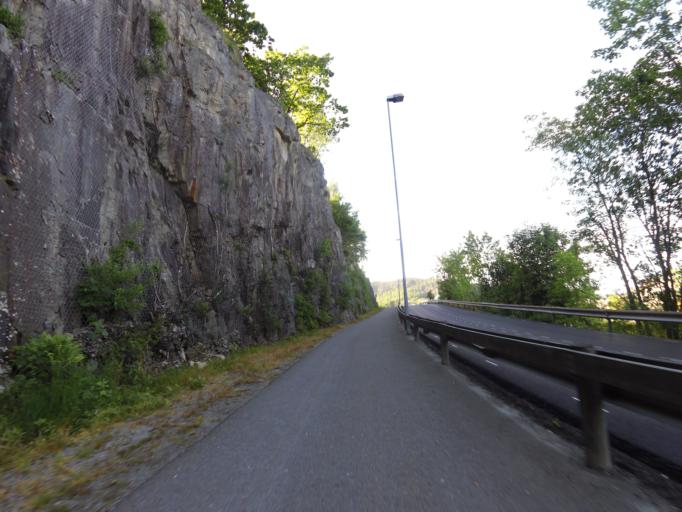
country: NO
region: Vest-Agder
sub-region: Flekkefjord
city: Flekkefjord
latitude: 58.2896
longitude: 6.6488
